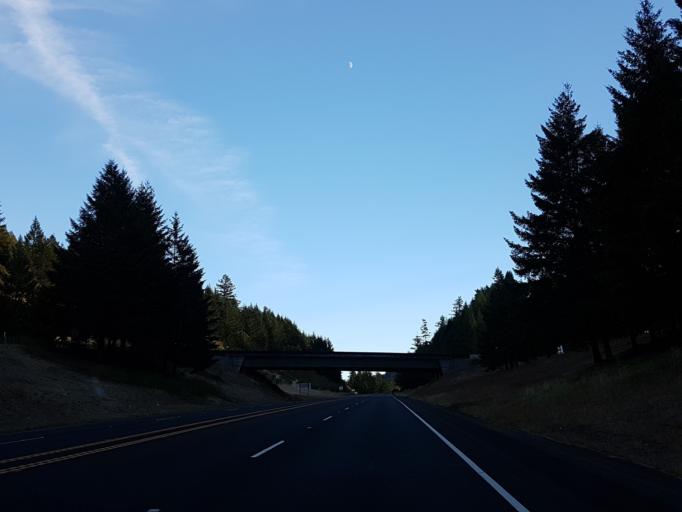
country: US
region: California
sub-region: Humboldt County
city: Redway
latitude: 39.9454
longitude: -123.7800
